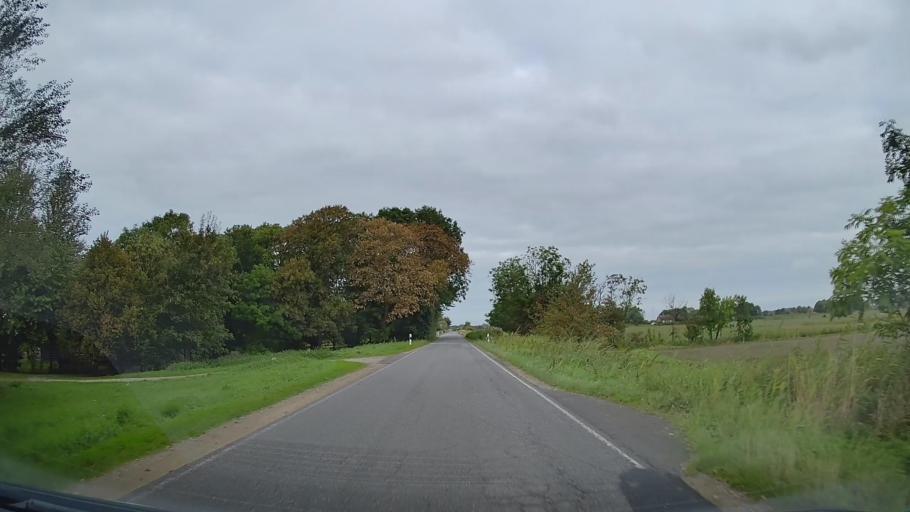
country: DE
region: Schleswig-Holstein
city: Emmelsbull-Horsbull
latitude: 54.7979
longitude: 8.7190
